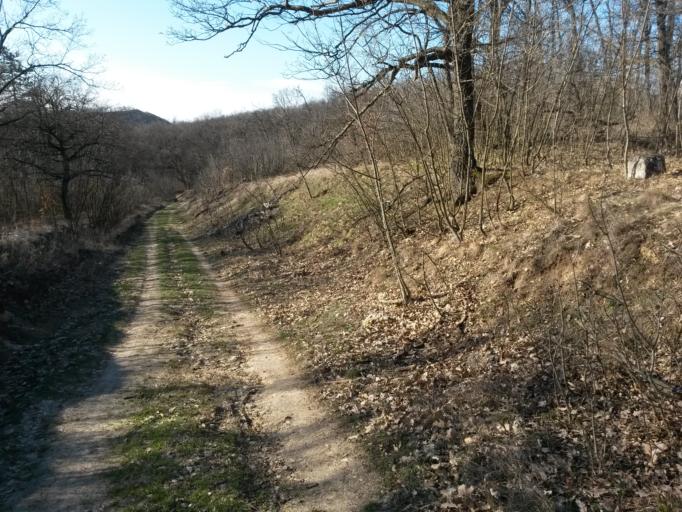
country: HU
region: Pest
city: Piliscsaba
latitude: 47.5988
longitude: 18.8181
